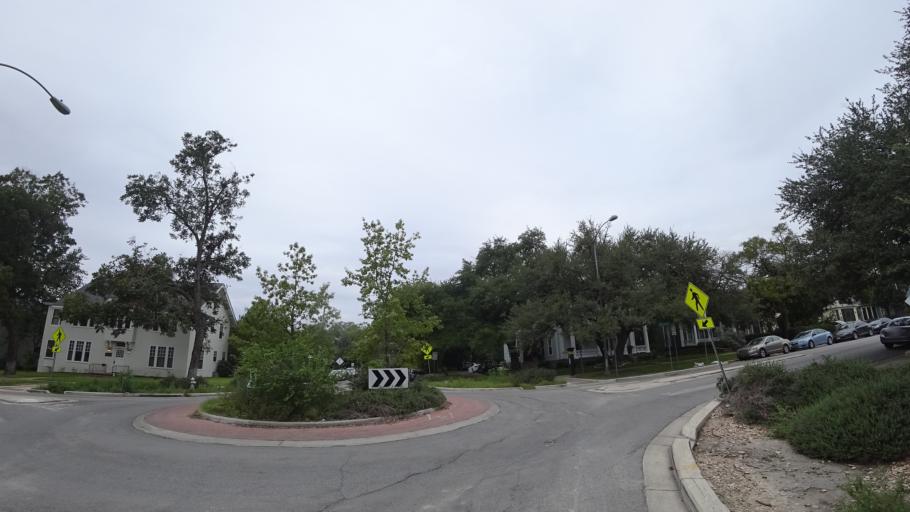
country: US
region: Texas
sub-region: Travis County
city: Austin
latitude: 30.2737
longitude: -97.7480
